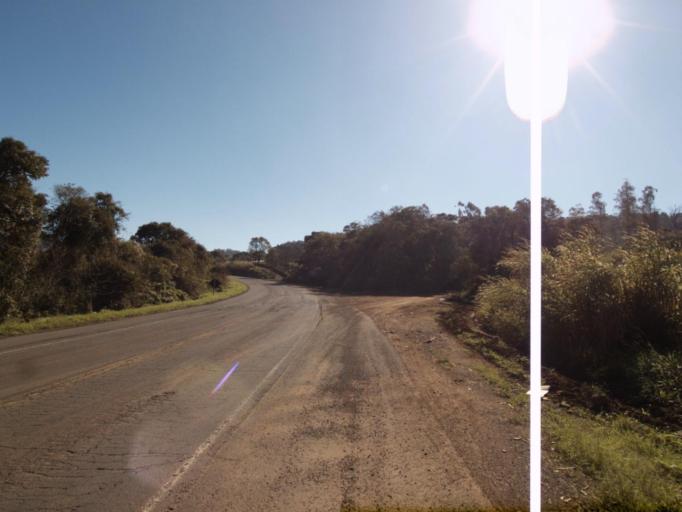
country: BR
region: Rio Grande do Sul
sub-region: Frederico Westphalen
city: Frederico Westphalen
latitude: -27.0442
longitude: -53.2256
